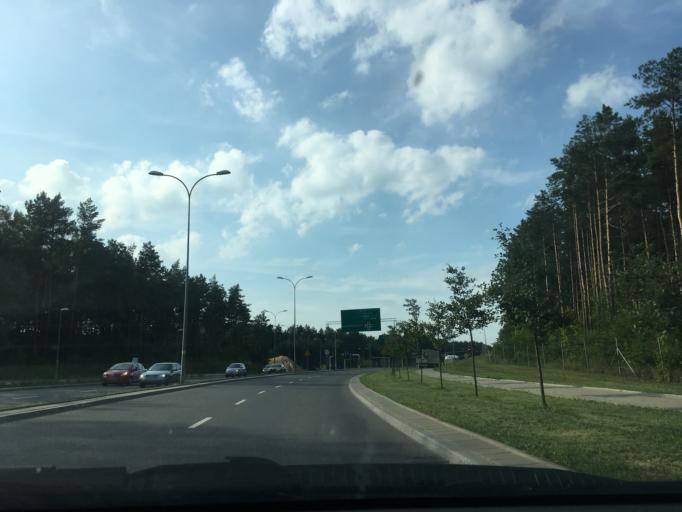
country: PL
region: Podlasie
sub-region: Bialystok
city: Bialystok
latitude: 53.1271
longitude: 23.2251
